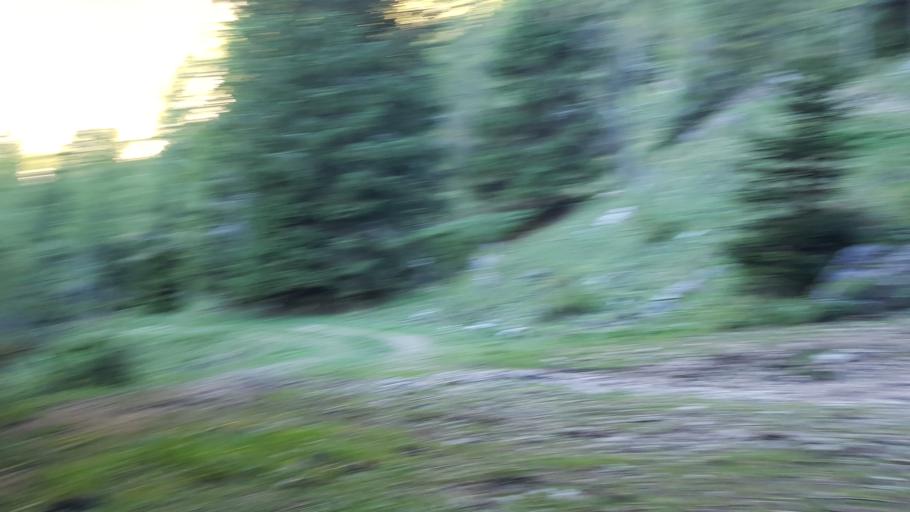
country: IT
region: Veneto
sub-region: Provincia di Belluno
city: Fusine
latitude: 46.3682
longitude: 12.0854
